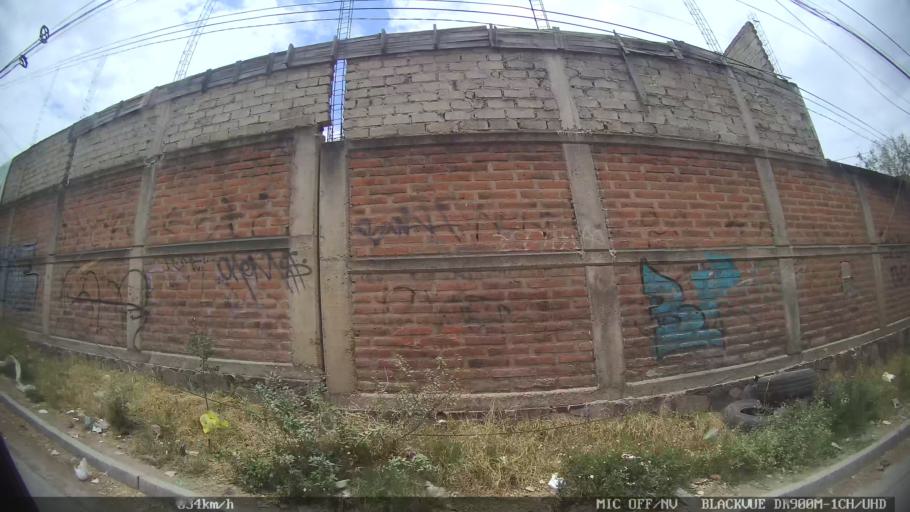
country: MX
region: Jalisco
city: Tlaquepaque
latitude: 20.6474
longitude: -103.2601
